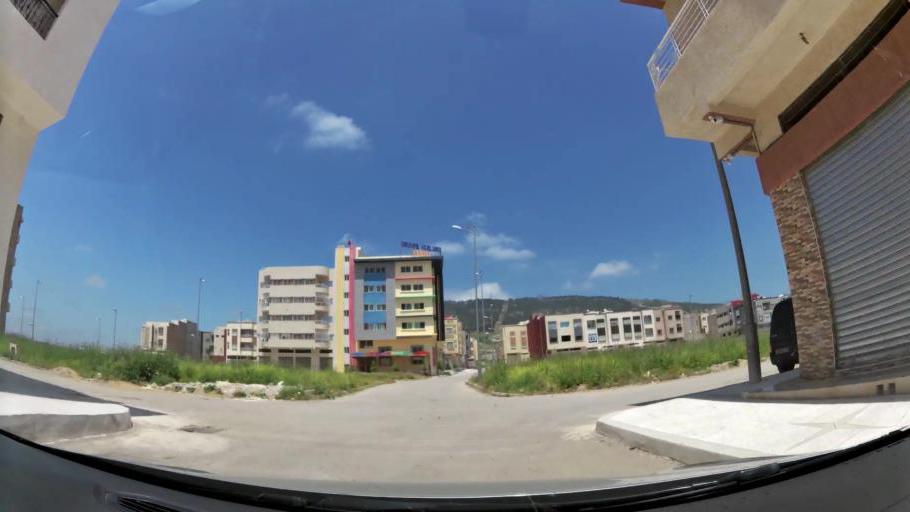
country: MA
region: Fes-Boulemane
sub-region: Fes
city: Fes
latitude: 34.0511
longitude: -5.0489
